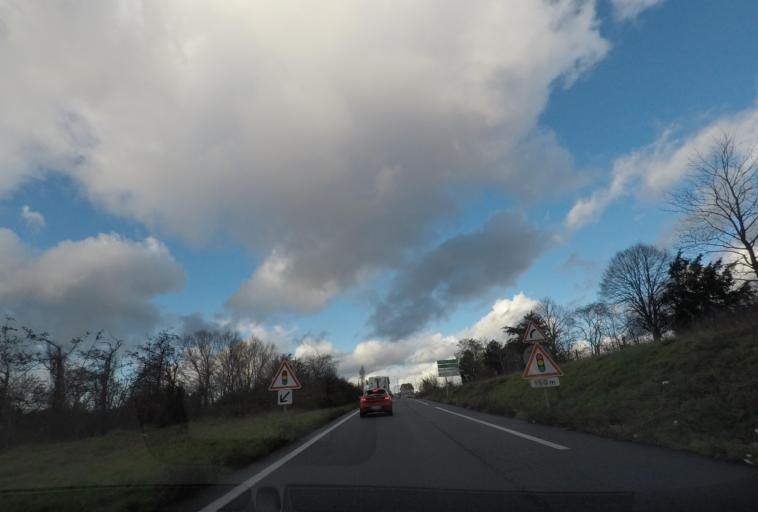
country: FR
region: Ile-de-France
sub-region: Departement de l'Essonne
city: Ormoy
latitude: 48.5707
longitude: 2.4700
